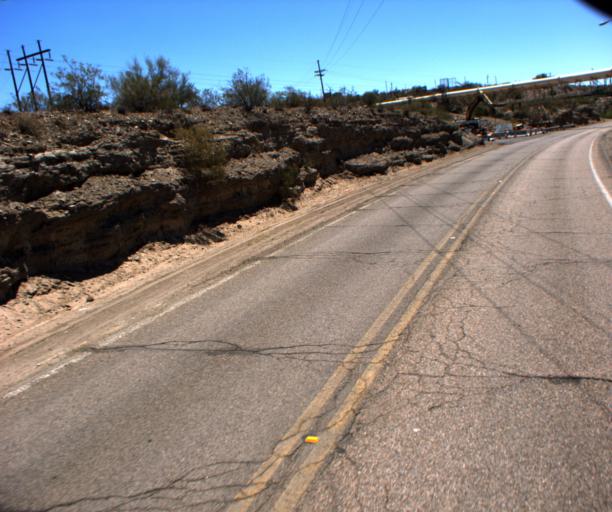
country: US
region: Arizona
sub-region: Pinal County
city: Kearny
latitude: 33.0025
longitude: -110.7908
